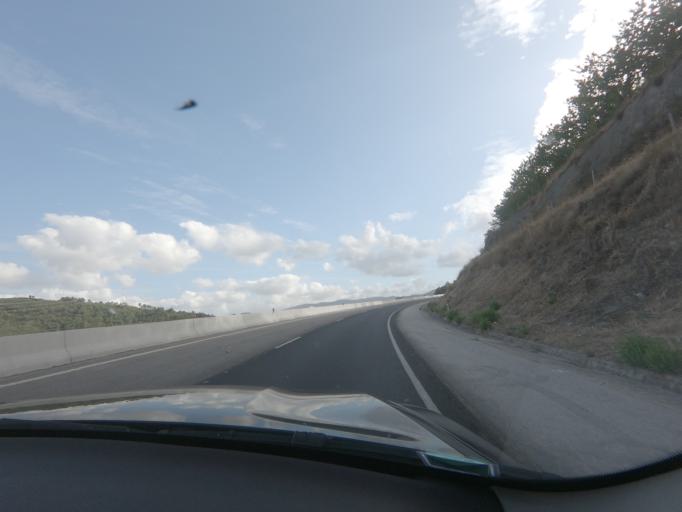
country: PT
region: Viseu
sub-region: Lamego
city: Lamego
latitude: 41.1028
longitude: -7.7748
